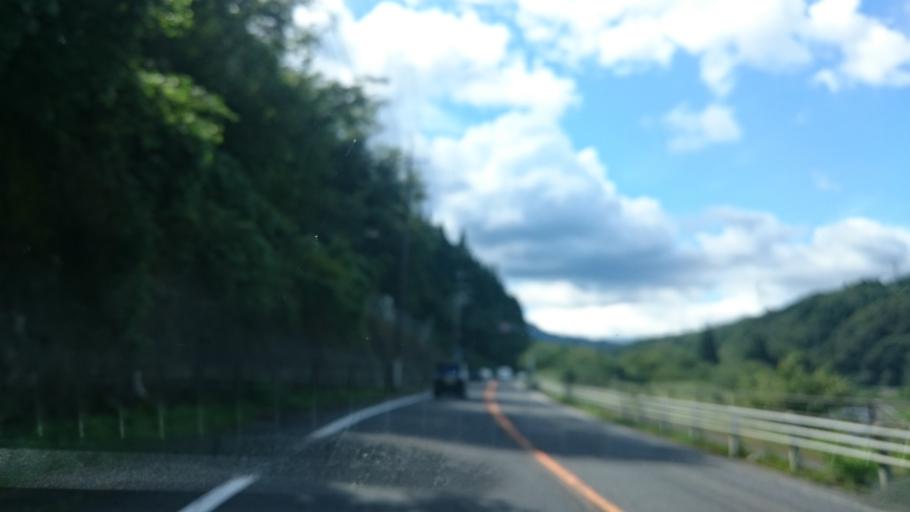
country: JP
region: Gifu
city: Nakatsugawa
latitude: 35.6284
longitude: 137.4569
